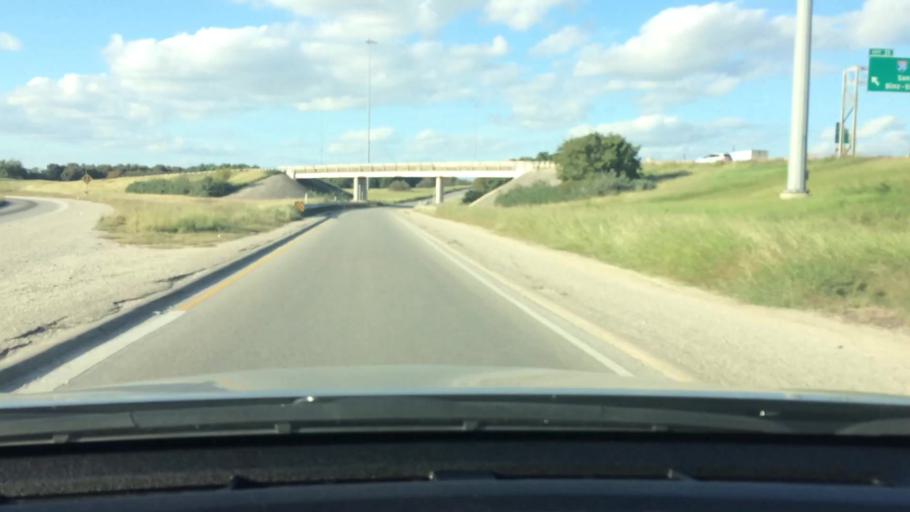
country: US
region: Texas
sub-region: Bexar County
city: Kirby
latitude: 29.4497
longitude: -98.4038
